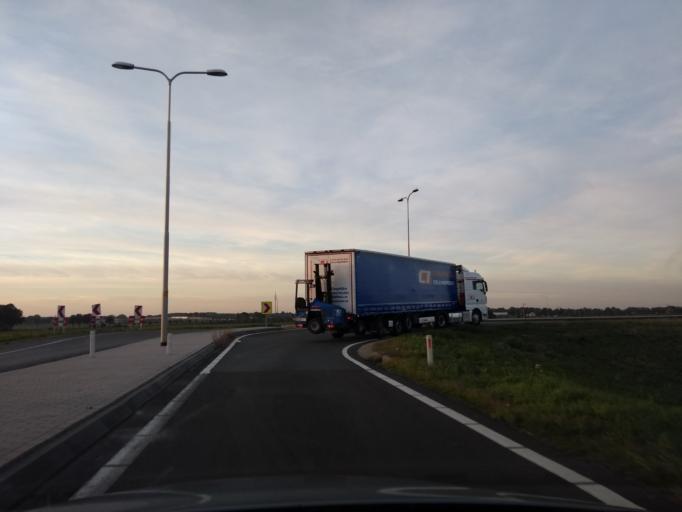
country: NL
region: Overijssel
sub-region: Gemeente Wierden
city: Wierden
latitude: 52.3420
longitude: 6.5960
